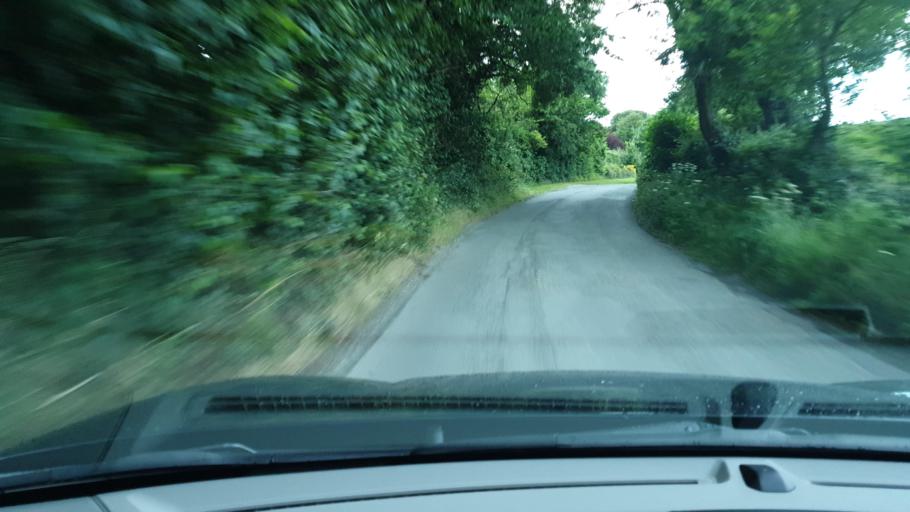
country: IE
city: Kentstown
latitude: 53.6018
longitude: -6.6016
